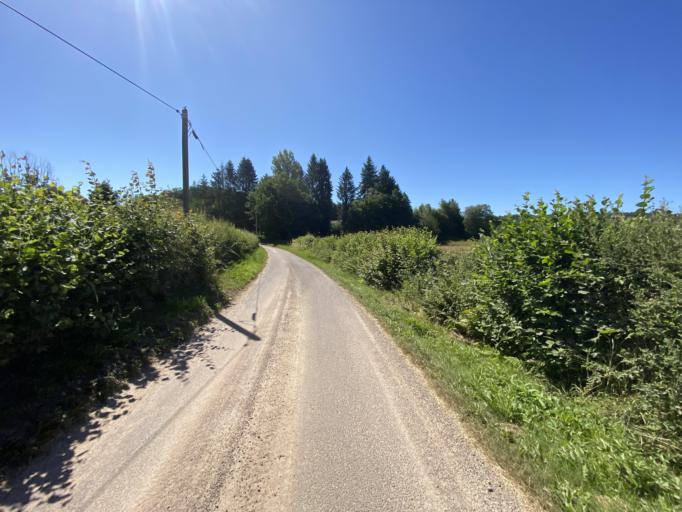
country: FR
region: Bourgogne
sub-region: Departement de la Cote-d'Or
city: Saulieu
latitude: 47.2974
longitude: 4.1187
